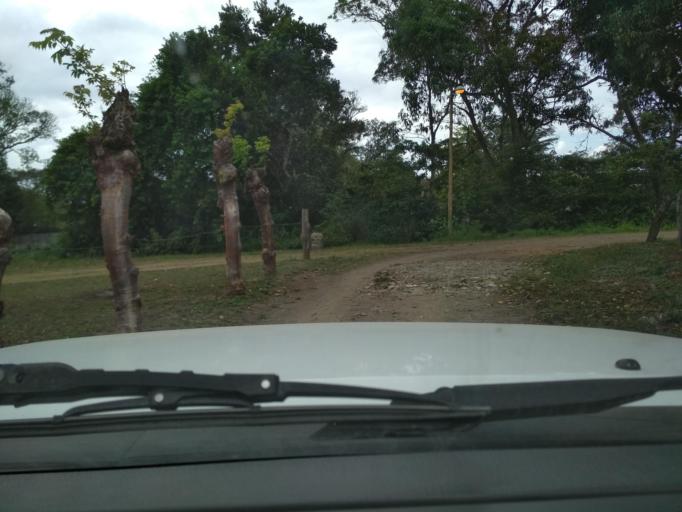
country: MX
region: Veracruz
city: El Tejar
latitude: 19.0582
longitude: -96.1538
